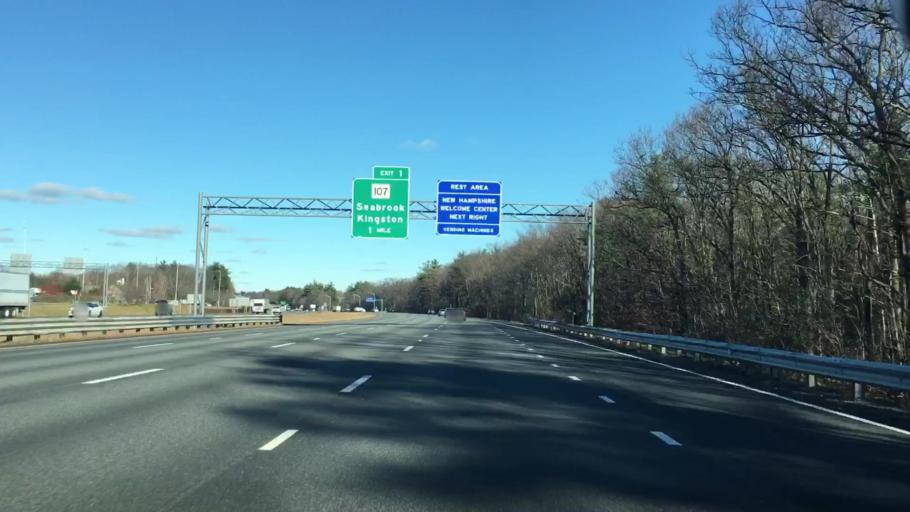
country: US
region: New Hampshire
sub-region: Rockingham County
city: Seabrook
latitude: 42.8767
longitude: -70.8848
